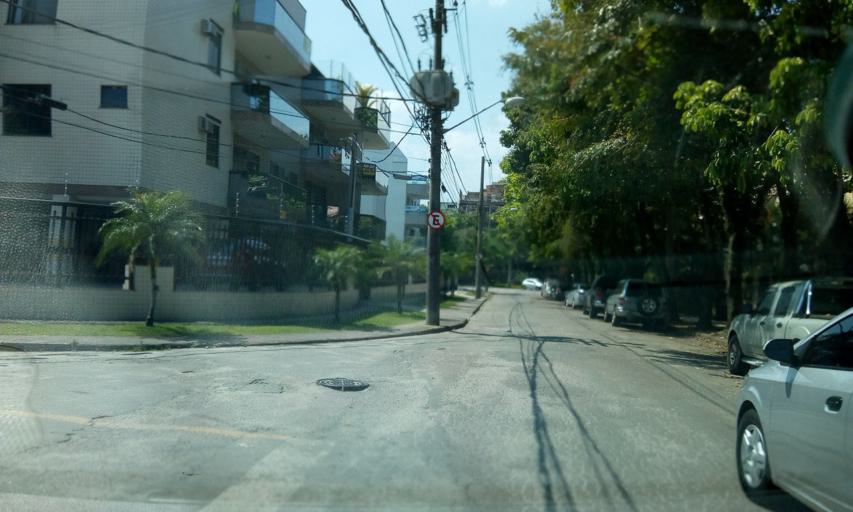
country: BR
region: Rio de Janeiro
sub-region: Nilopolis
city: Nilopolis
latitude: -23.0225
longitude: -43.4778
